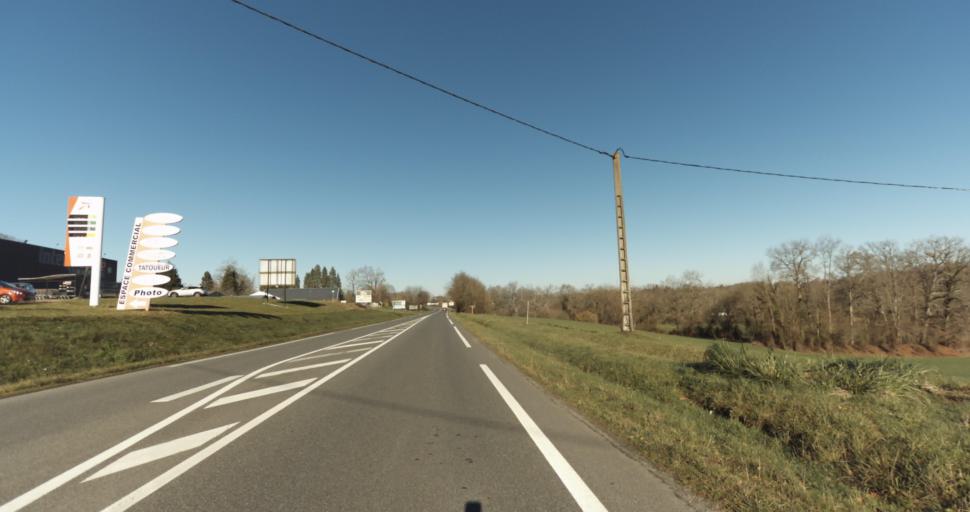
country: FR
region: Aquitaine
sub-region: Departement des Pyrenees-Atlantiques
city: Morlaas
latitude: 43.3468
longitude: -0.2542
